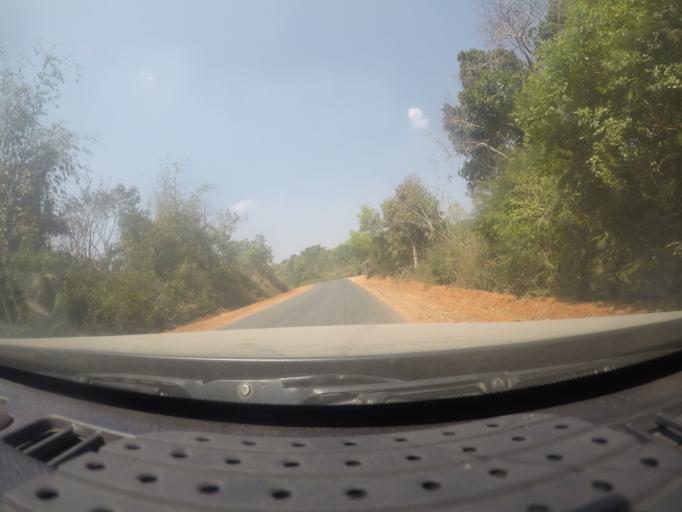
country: MM
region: Shan
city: Taunggyi
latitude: 20.9960
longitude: 96.5333
